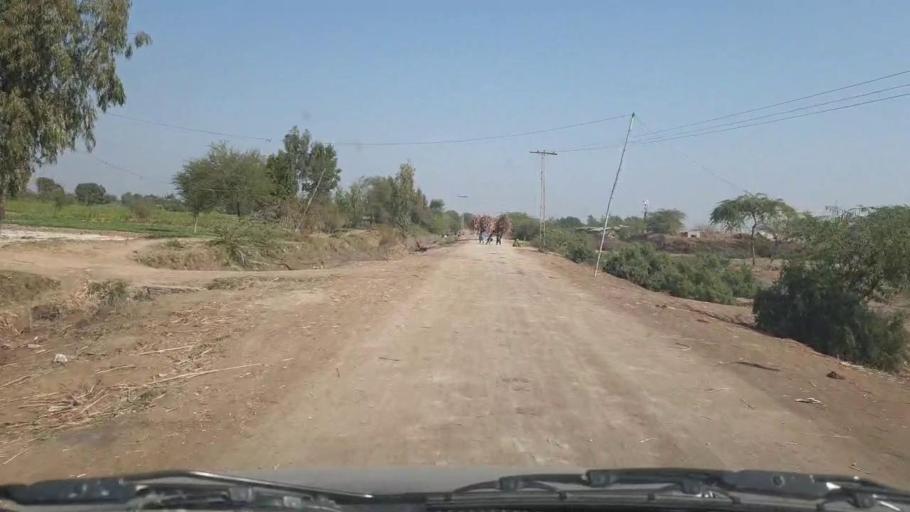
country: PK
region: Sindh
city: Samaro
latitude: 25.2945
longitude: 69.2907
